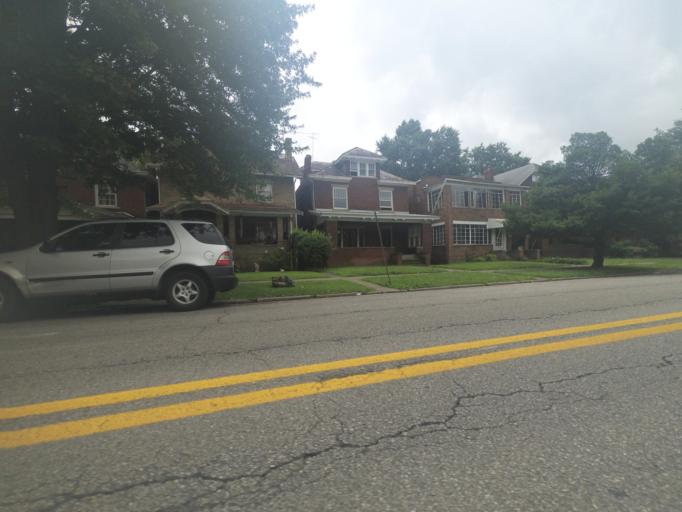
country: US
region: West Virginia
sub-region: Cabell County
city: Huntington
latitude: 38.4148
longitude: -82.4356
